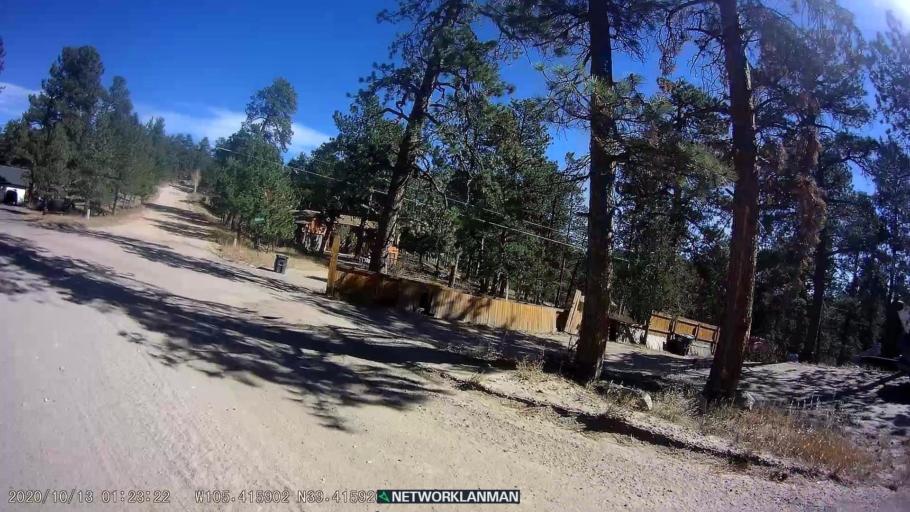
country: US
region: Colorado
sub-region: Jefferson County
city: Evergreen
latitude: 39.4173
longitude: -105.4170
